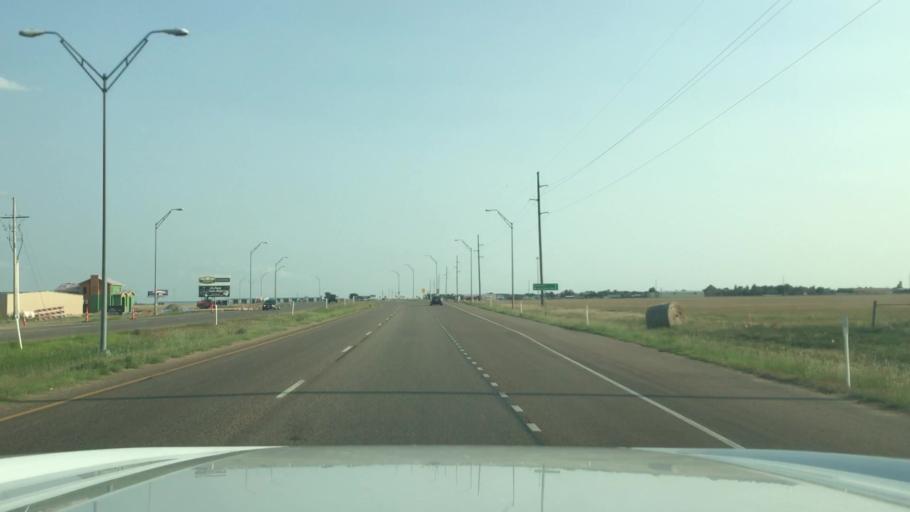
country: US
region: Texas
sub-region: Potter County
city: Bushland
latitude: 35.1248
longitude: -101.9381
